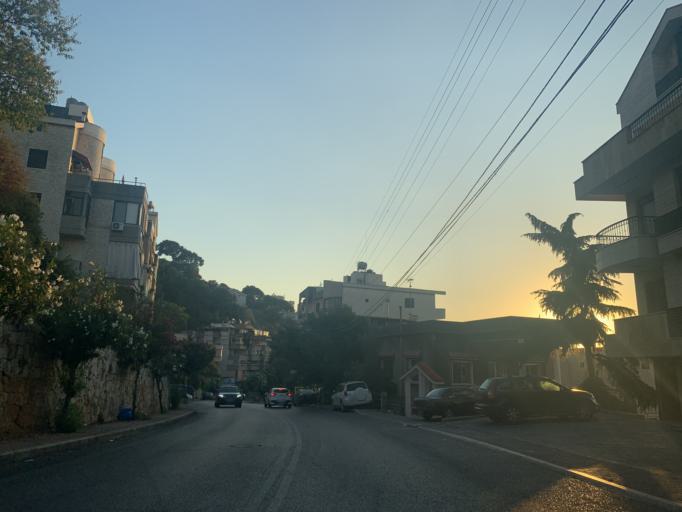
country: LB
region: Mont-Liban
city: Djounie
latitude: 33.9565
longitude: 35.6426
